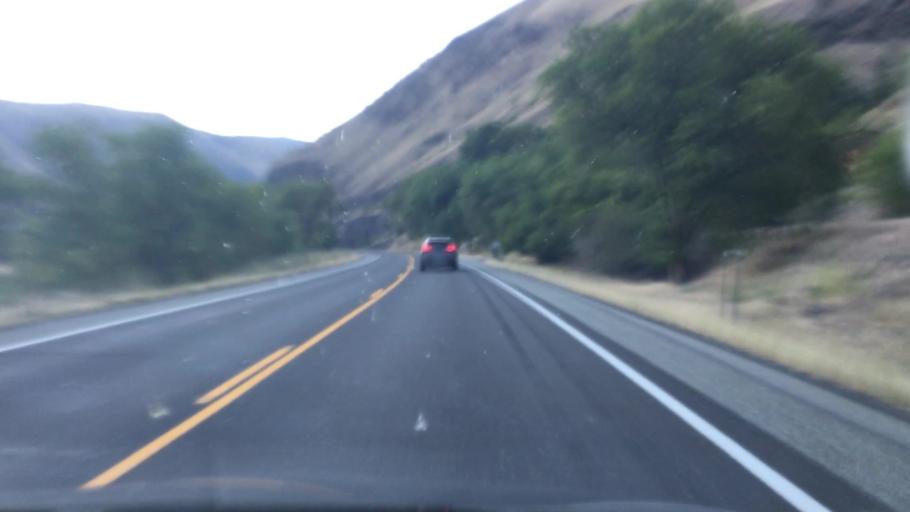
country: US
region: Idaho
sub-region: Valley County
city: McCall
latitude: 45.3401
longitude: -116.3483
